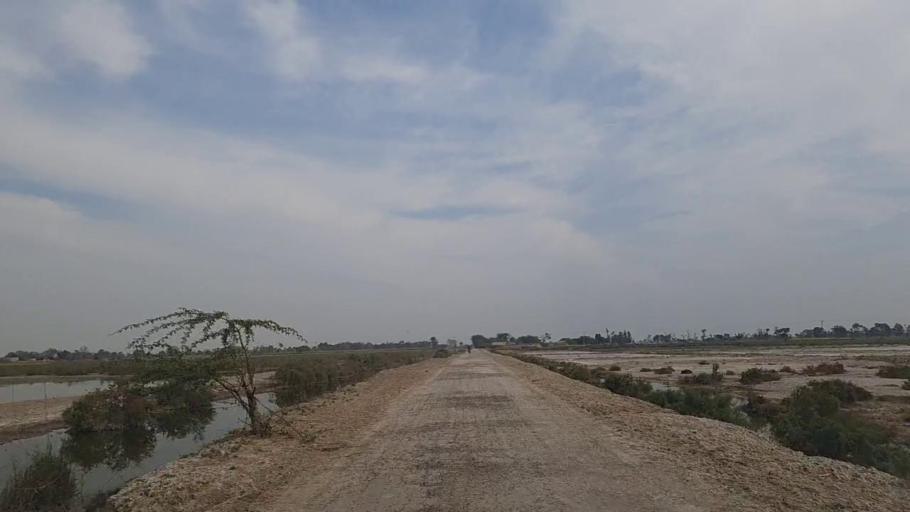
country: PK
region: Sindh
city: Daur
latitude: 26.4994
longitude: 68.3857
